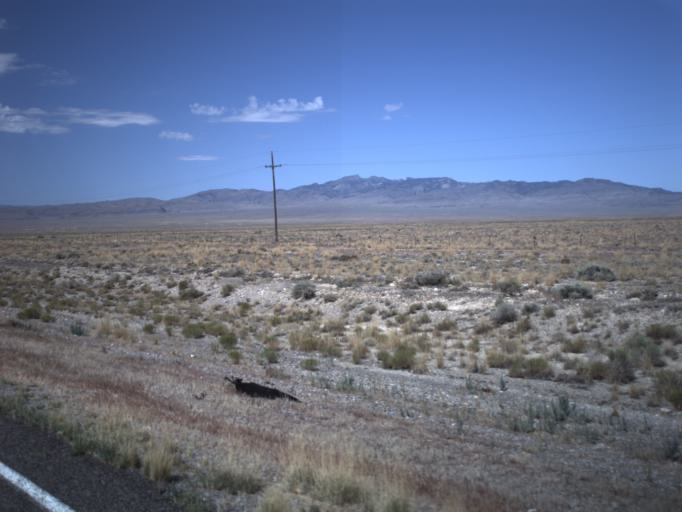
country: US
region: Utah
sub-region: Millard County
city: Delta
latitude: 39.1369
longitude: -113.0920
